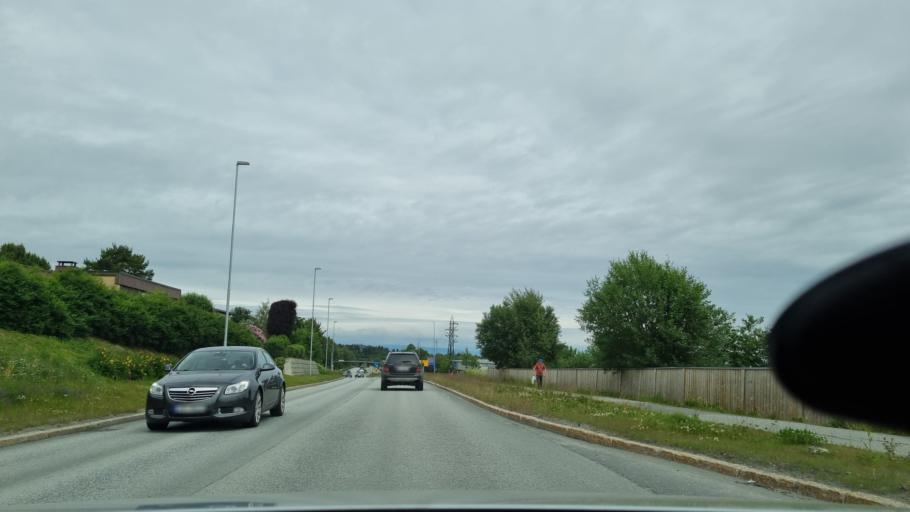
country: NO
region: Sor-Trondelag
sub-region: Trondheim
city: Trondheim
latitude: 63.3649
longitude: 10.3437
